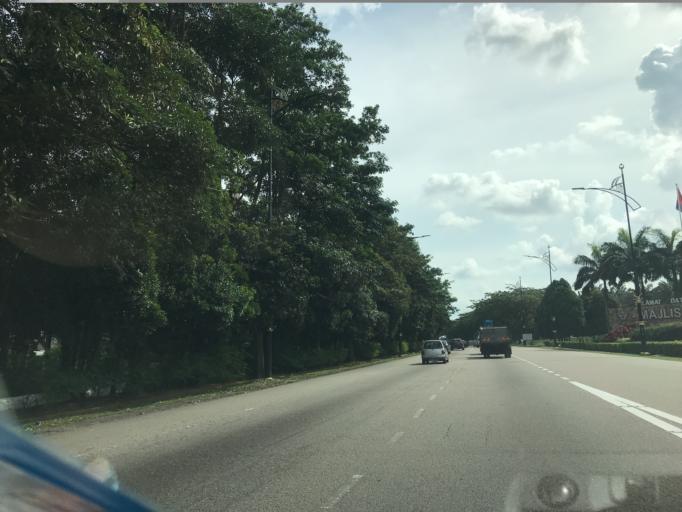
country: MY
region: Johor
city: Skudai
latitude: 1.5580
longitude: 103.6593
